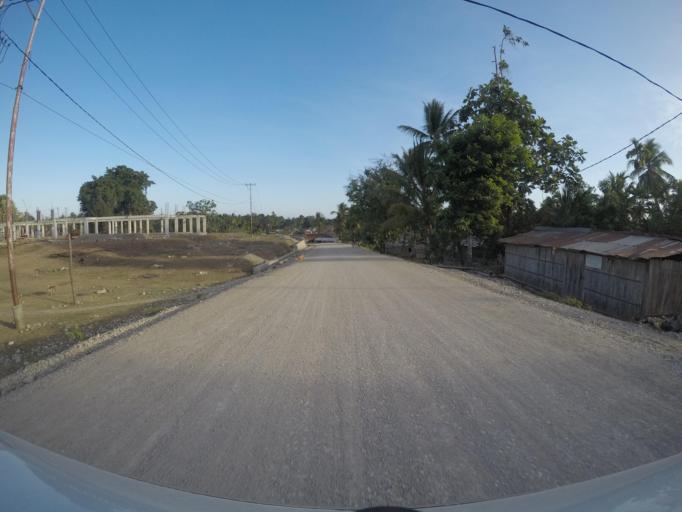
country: TL
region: Viqueque
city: Viqueque
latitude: -8.8482
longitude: 126.5125
